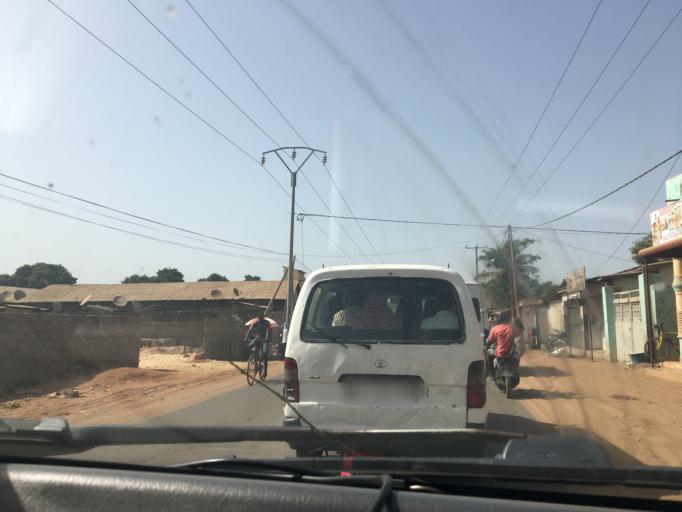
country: GM
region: Western
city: Abuko
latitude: 13.3993
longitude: -16.6733
